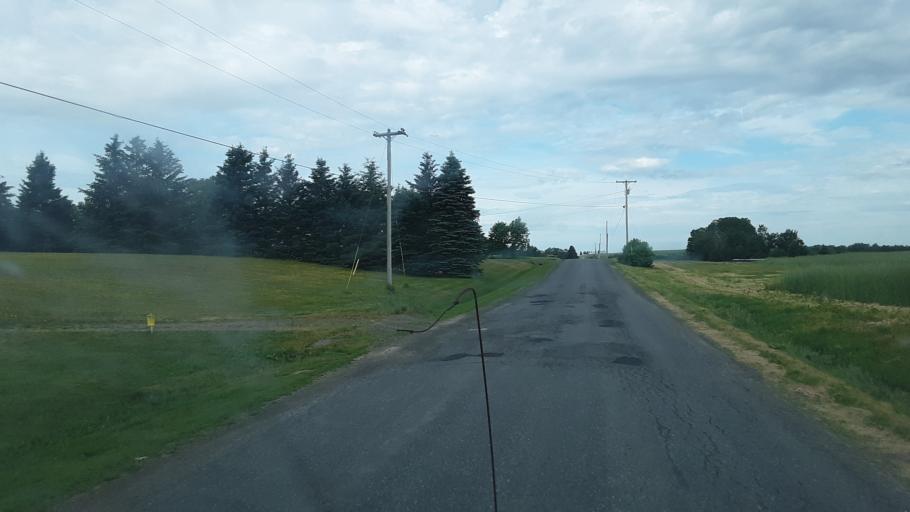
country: US
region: Maine
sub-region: Aroostook County
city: Caribou
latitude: 46.8112
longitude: -68.0147
